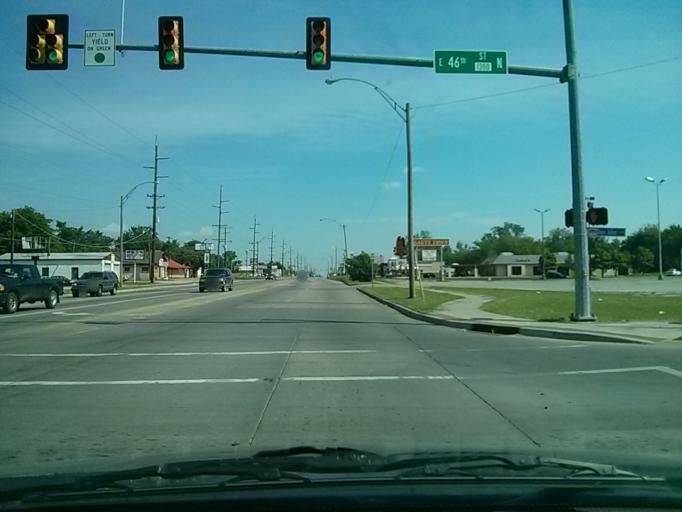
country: US
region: Oklahoma
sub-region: Tulsa County
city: Turley
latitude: 36.2205
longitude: -95.9754
